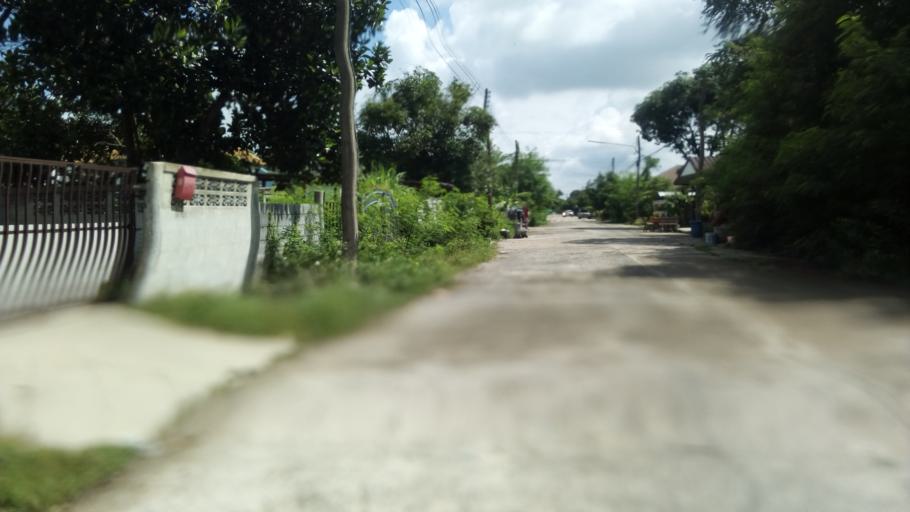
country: TH
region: Pathum Thani
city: Nong Suea
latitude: 14.0507
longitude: 100.8625
